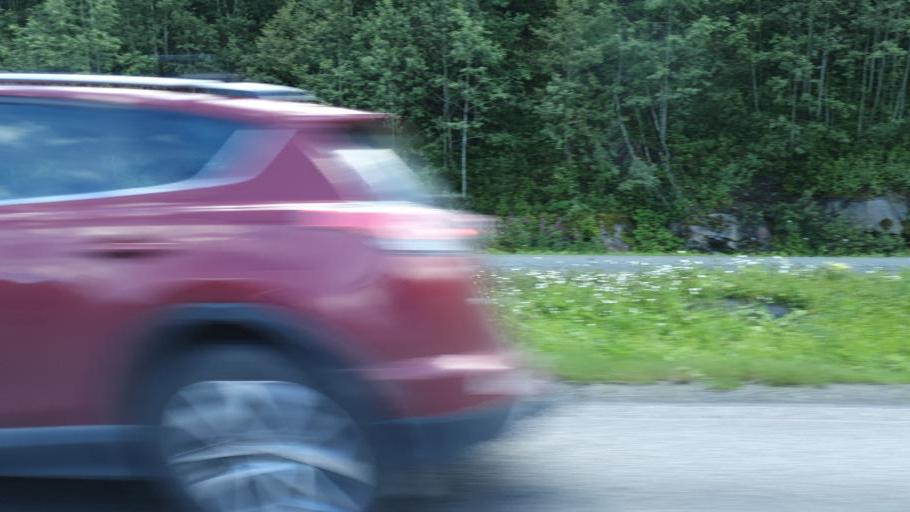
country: NO
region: Sor-Trondelag
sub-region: Midtre Gauldal
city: Storen
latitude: 62.9828
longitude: 10.2369
